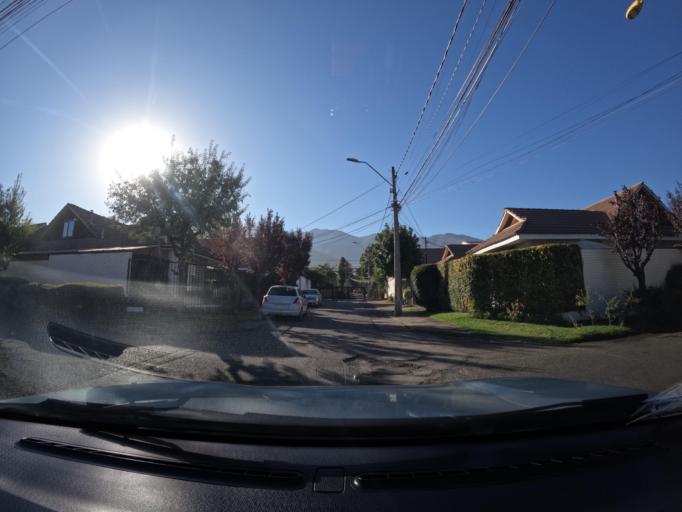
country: CL
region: Santiago Metropolitan
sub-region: Provincia de Santiago
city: Villa Presidente Frei, Nunoa, Santiago, Chile
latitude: -33.4799
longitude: -70.5504
